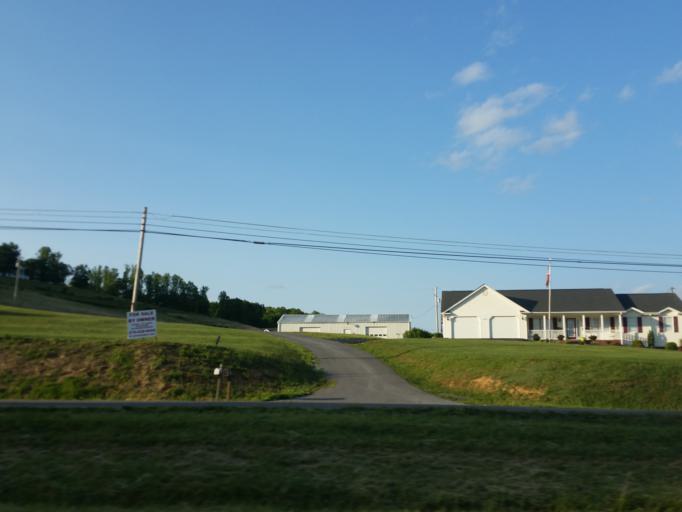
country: US
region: Virginia
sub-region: Washington County
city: Abingdon
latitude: 36.7268
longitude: -82.0244
